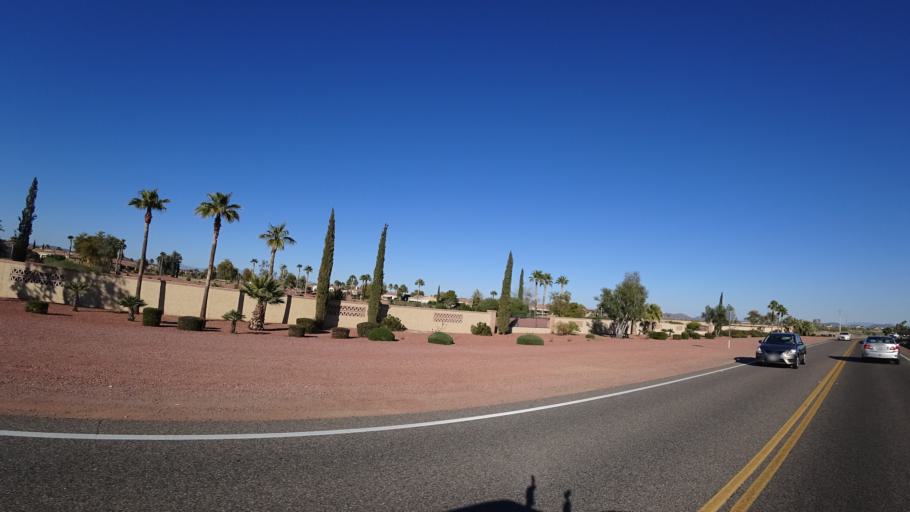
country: US
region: Arizona
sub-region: Maricopa County
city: Sun City West
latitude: 33.6820
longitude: -112.3363
